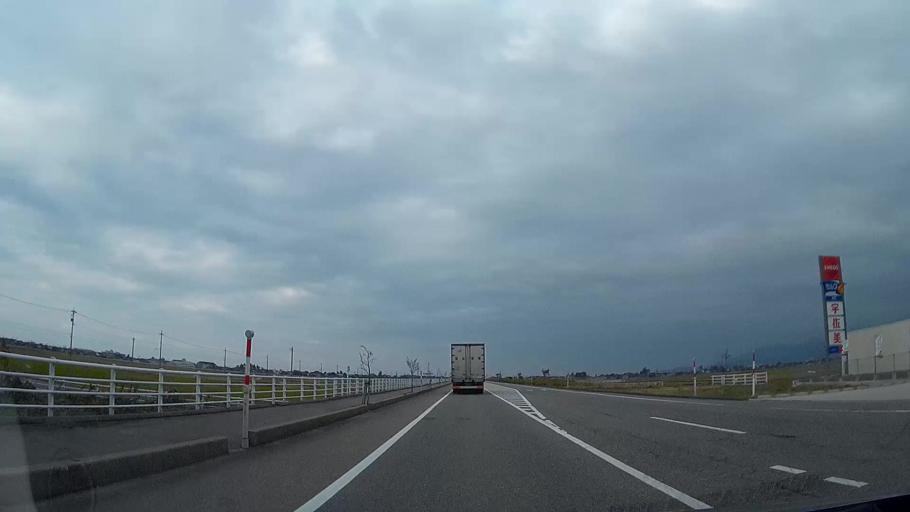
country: JP
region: Toyama
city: Nyuzen
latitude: 36.9135
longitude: 137.4591
